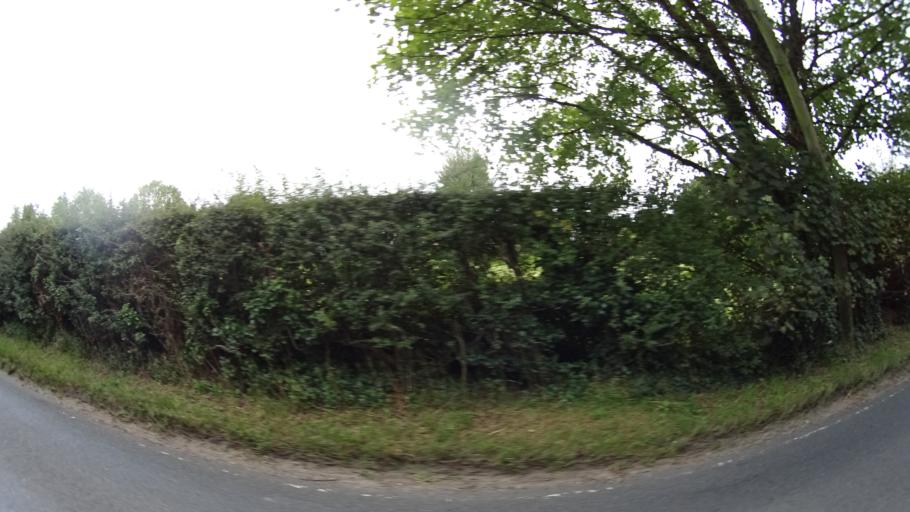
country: GB
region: England
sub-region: Dorset
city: Shaftesbury
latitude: 51.0105
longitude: -2.2031
